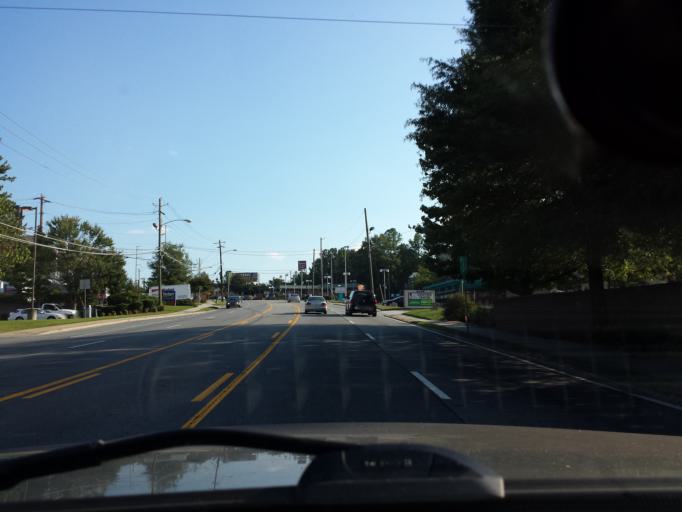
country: US
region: Georgia
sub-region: Fulton County
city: Sandy Springs
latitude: 33.9332
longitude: -84.3801
